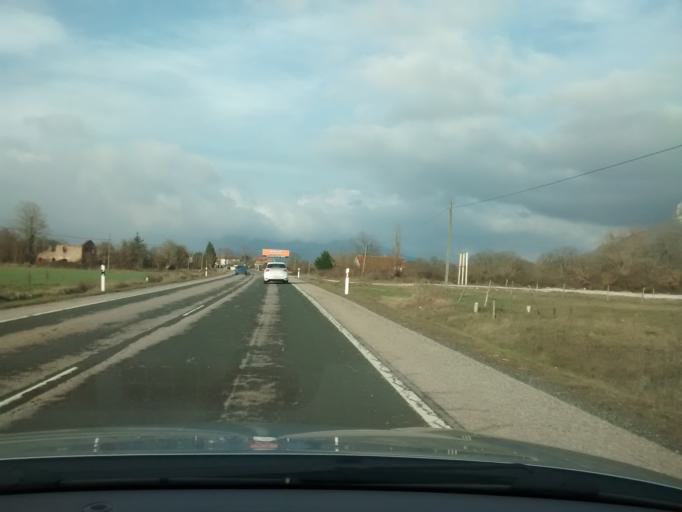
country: ES
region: Castille and Leon
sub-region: Provincia de Burgos
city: Espinosa de los Monteros
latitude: 43.0591
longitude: -3.4774
